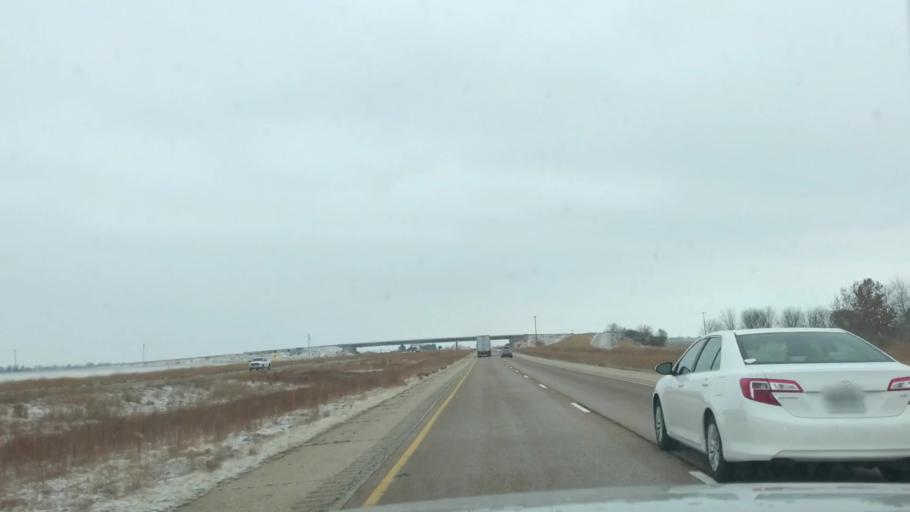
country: US
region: Illinois
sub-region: Montgomery County
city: Raymond
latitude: 39.3742
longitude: -89.6428
